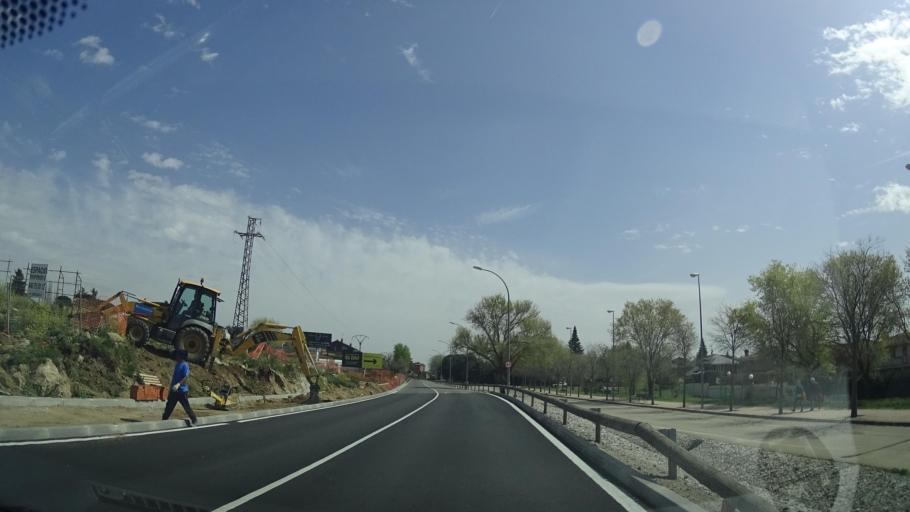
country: ES
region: Madrid
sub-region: Provincia de Madrid
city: Colmenar Viejo
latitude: 40.6755
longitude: -3.7790
